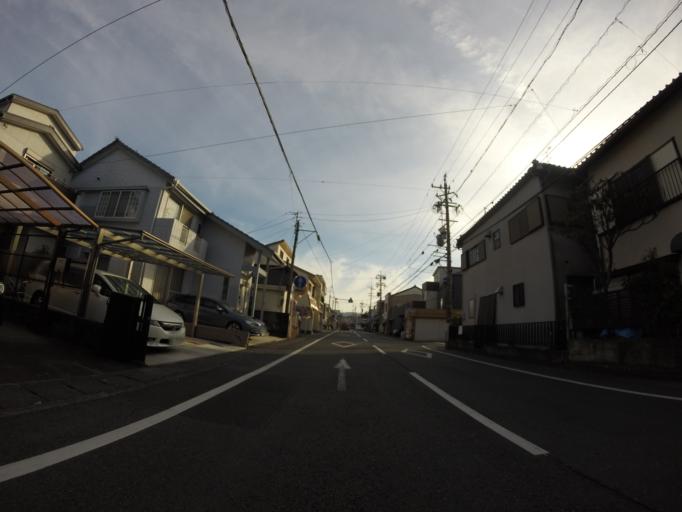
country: JP
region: Shizuoka
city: Shizuoka-shi
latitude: 35.0303
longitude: 138.4827
